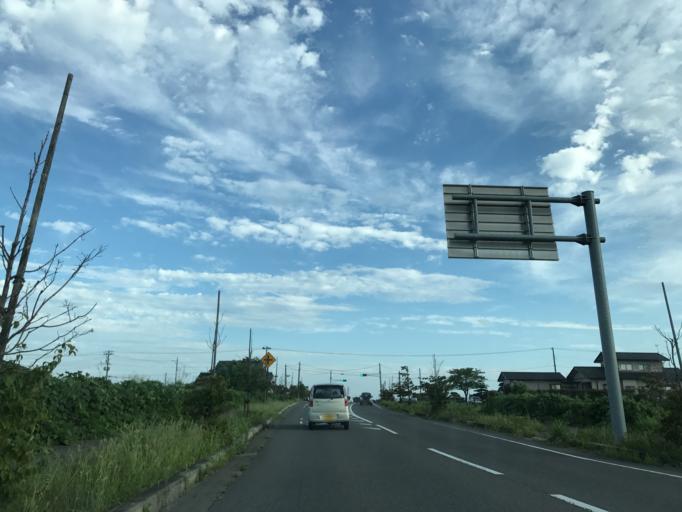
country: JP
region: Fukushima
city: Koriyama
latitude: 37.3459
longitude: 140.3348
